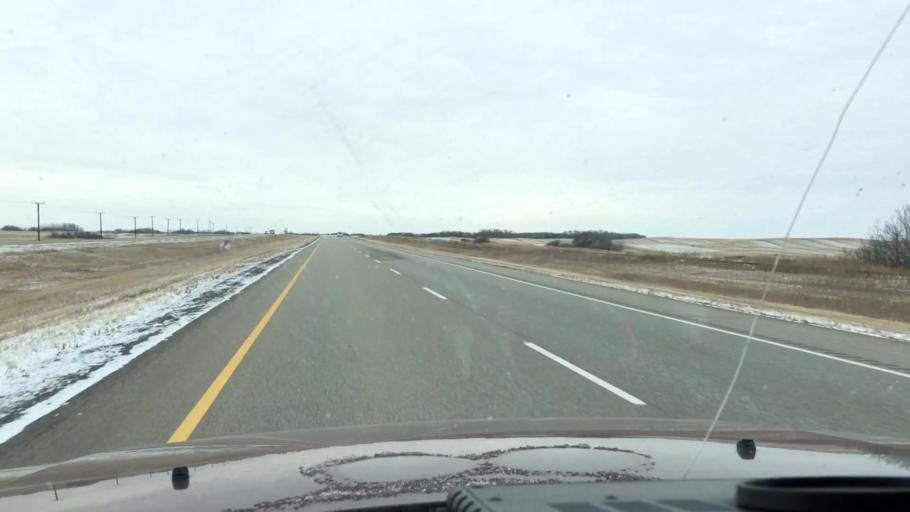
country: CA
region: Saskatchewan
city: Watrous
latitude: 51.3959
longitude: -106.1726
